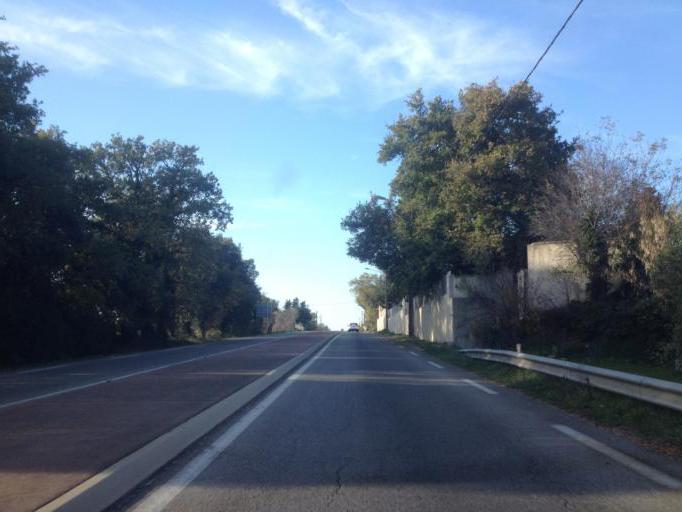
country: FR
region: Provence-Alpes-Cote d'Azur
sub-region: Departement du Vaucluse
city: Courthezon
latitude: 44.0925
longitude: 4.8768
